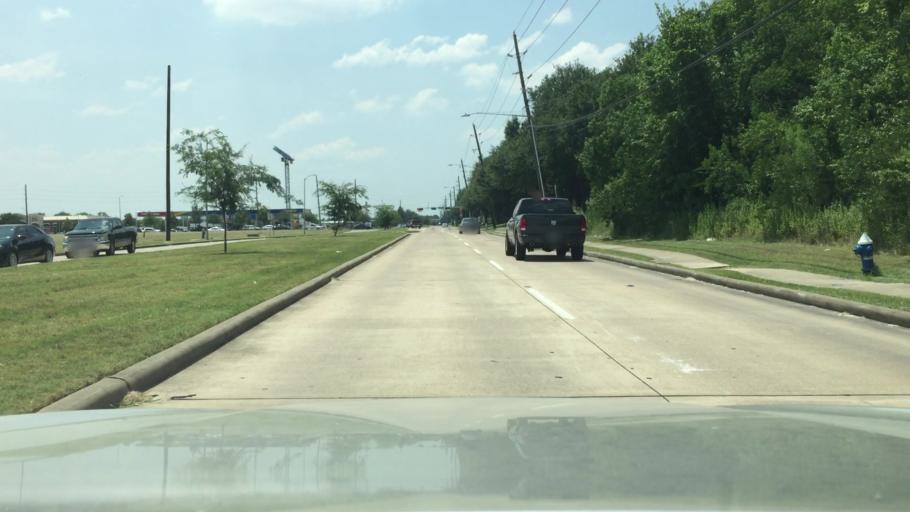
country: US
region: Texas
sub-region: Harris County
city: Bunker Hill Village
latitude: 29.7267
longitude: -95.5925
